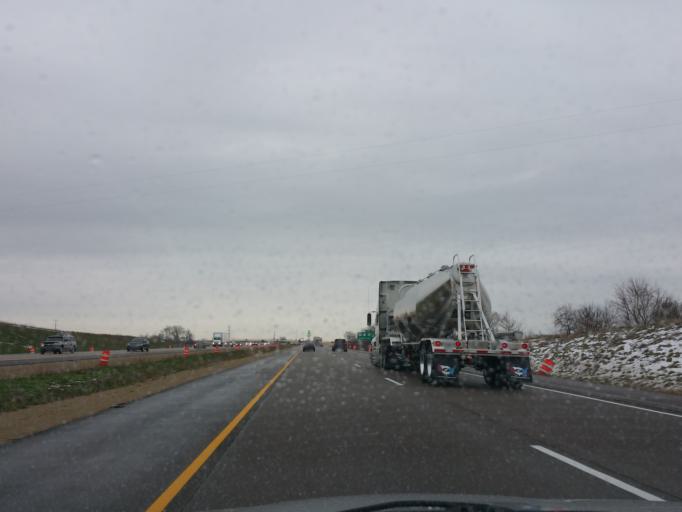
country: US
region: Wisconsin
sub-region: Rock County
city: Edgerton
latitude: 42.8805
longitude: -89.0633
